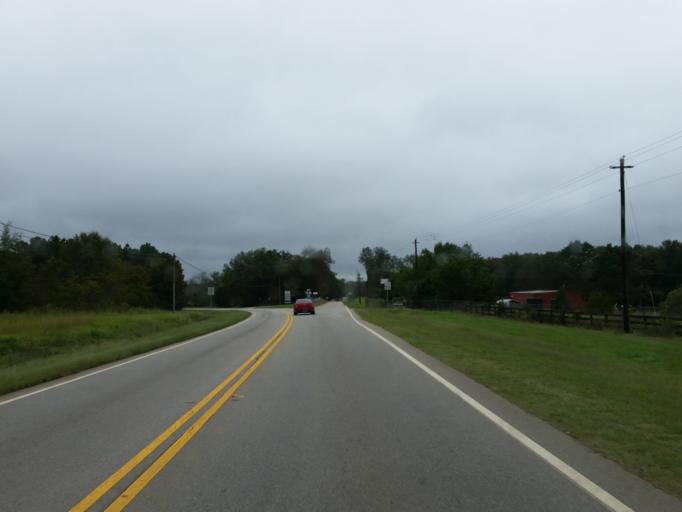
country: US
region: Georgia
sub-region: Crawford County
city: Roberta
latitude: 32.8769
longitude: -84.0908
